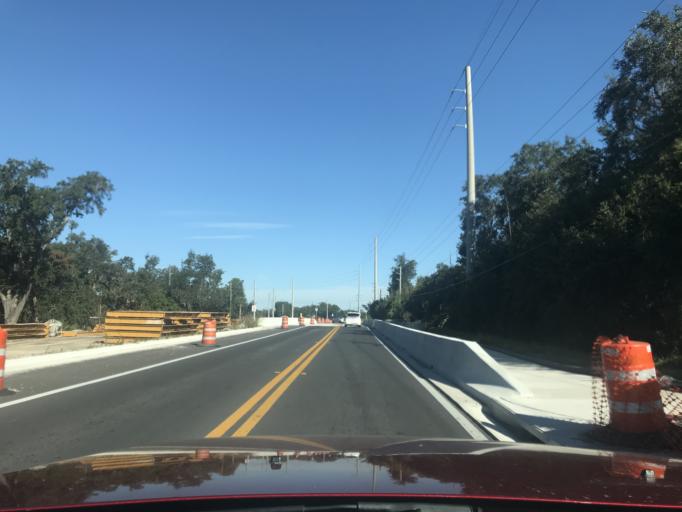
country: US
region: Florida
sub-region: Osceola County
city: Campbell
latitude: 28.2666
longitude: -81.4359
